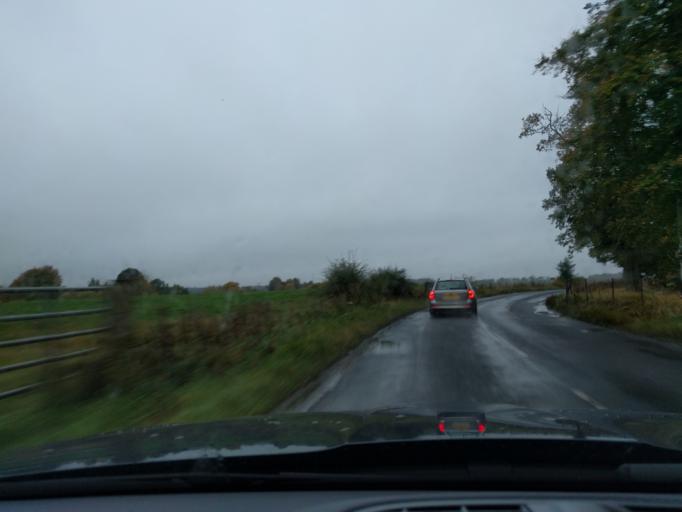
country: GB
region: Scotland
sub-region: The Scottish Borders
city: Allanton
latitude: 55.7204
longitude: -2.1477
